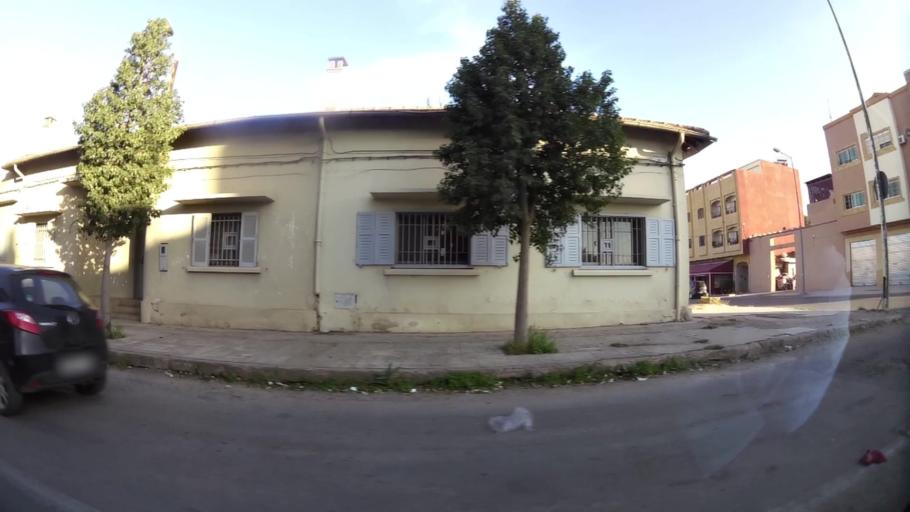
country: MA
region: Oriental
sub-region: Oujda-Angad
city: Oujda
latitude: 34.6946
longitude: -1.9083
